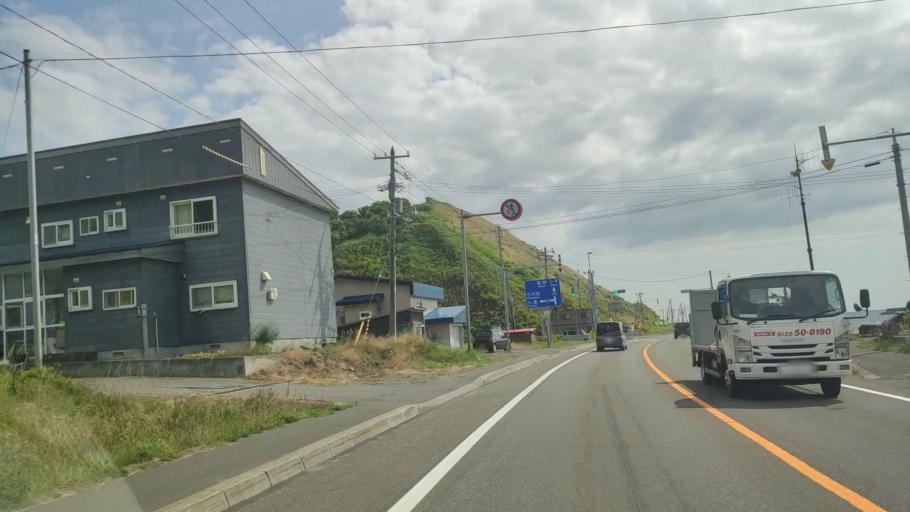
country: JP
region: Hokkaido
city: Rumoi
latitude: 44.2299
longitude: 141.6566
